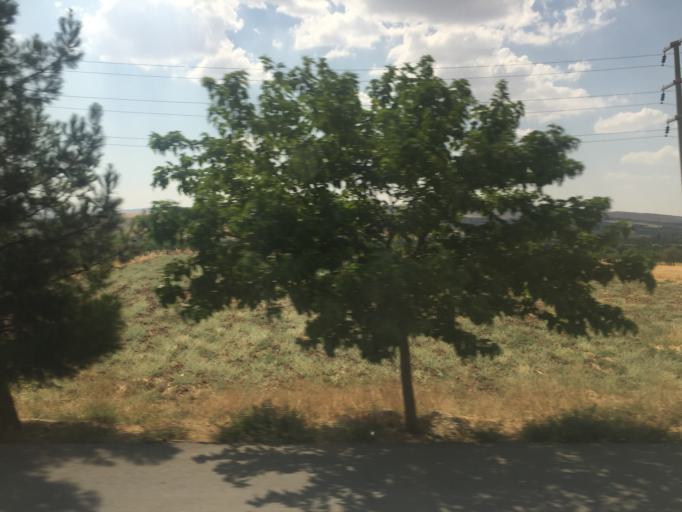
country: TR
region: Sanliurfa
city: Sanliurfa
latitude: 37.2433
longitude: 38.7937
